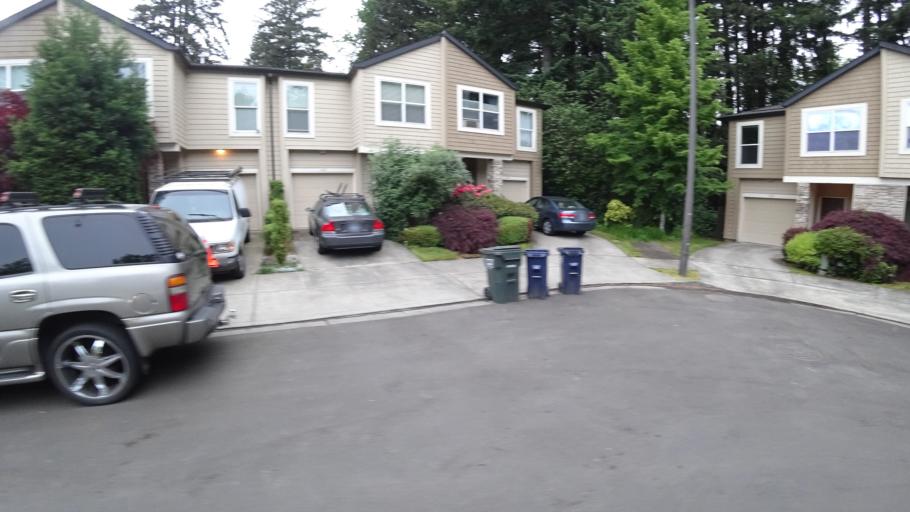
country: US
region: Oregon
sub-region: Washington County
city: Rockcreek
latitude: 45.5283
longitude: -122.8956
